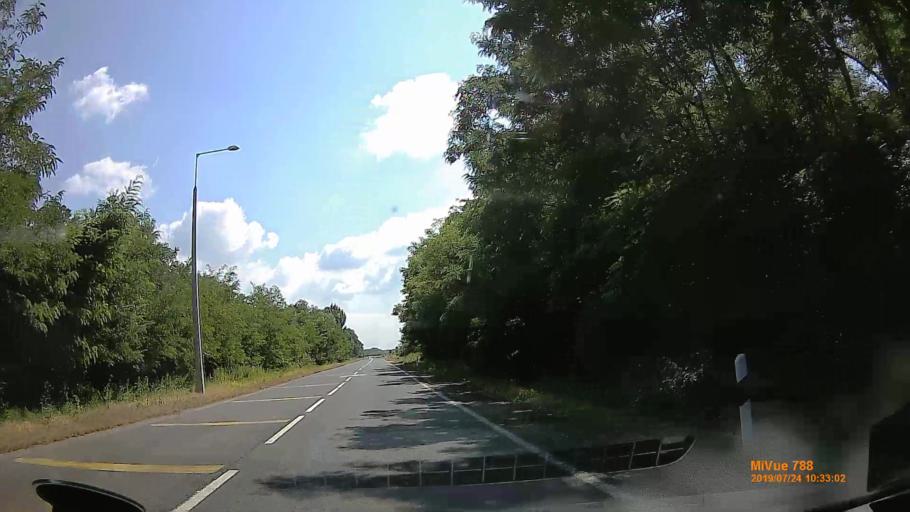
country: HU
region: Szabolcs-Szatmar-Bereg
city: Tarpa
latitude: 48.1590
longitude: 22.5439
